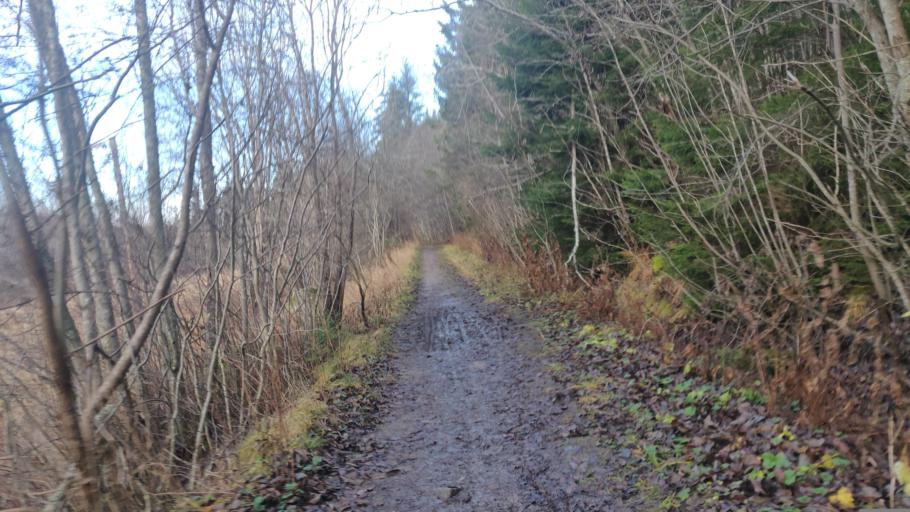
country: SE
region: Vaesternorrland
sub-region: Sundsvalls Kommun
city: Nolby
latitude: 62.3027
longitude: 17.3560
